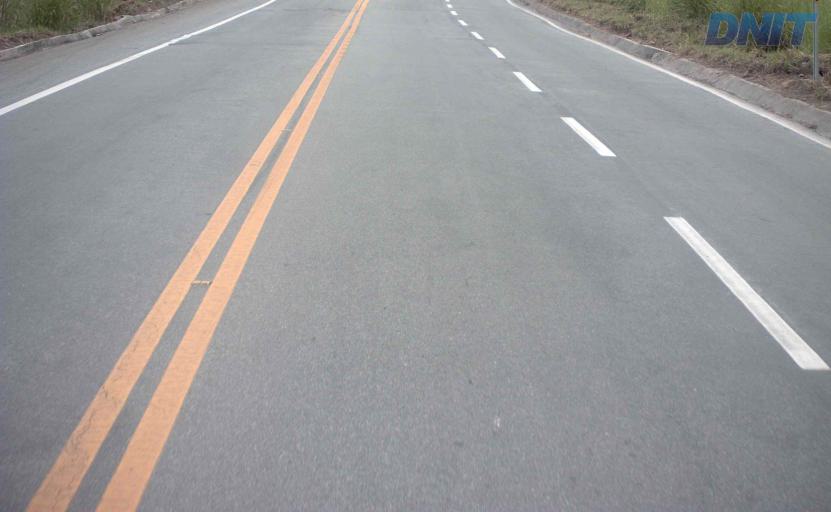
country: BR
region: Minas Gerais
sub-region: Timoteo
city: Timoteo
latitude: -19.6395
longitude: -42.8190
